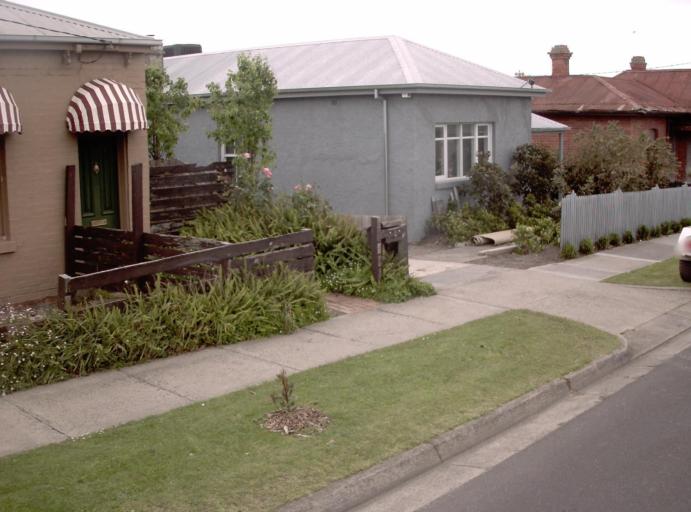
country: AU
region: Victoria
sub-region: Maroondah
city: Ringwood East
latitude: -37.8190
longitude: 145.2273
